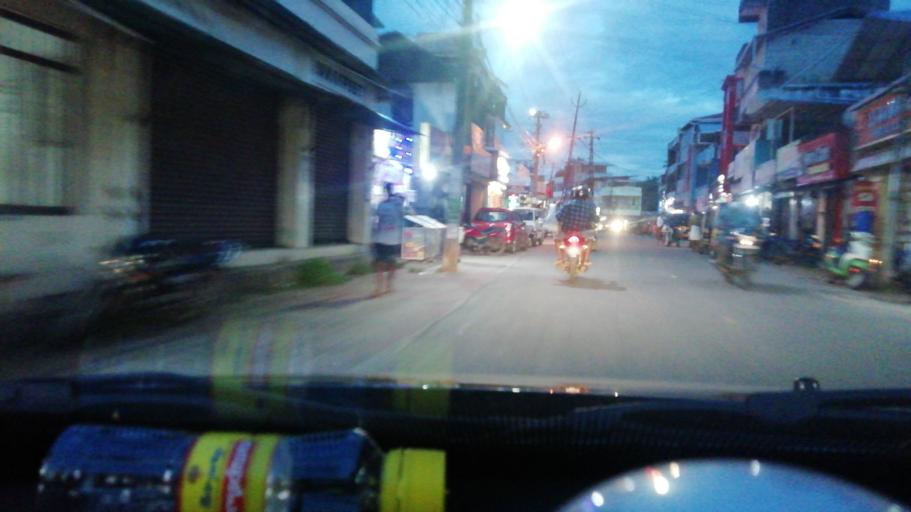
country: IN
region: Kerala
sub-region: Thiruvananthapuram
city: Paravur
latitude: 8.8105
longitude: 76.6693
